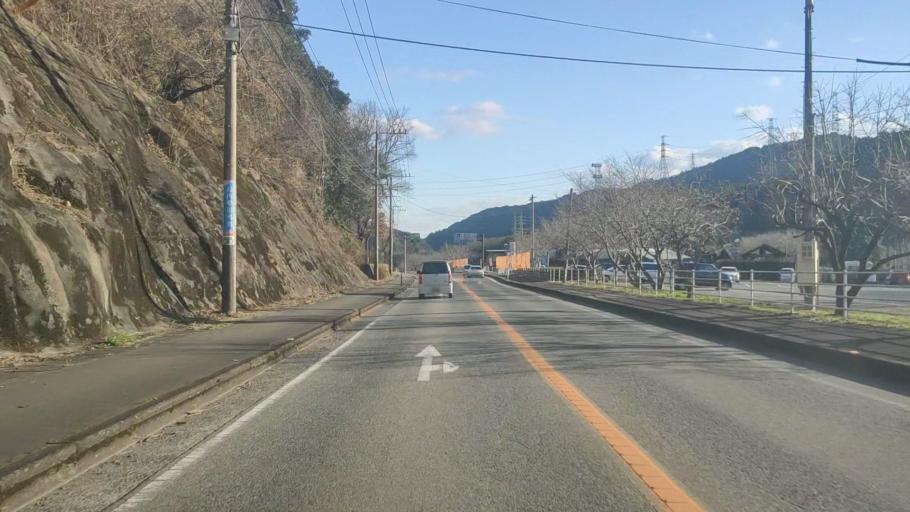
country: JP
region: Saga Prefecture
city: Saga-shi
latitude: 33.3409
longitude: 130.2569
